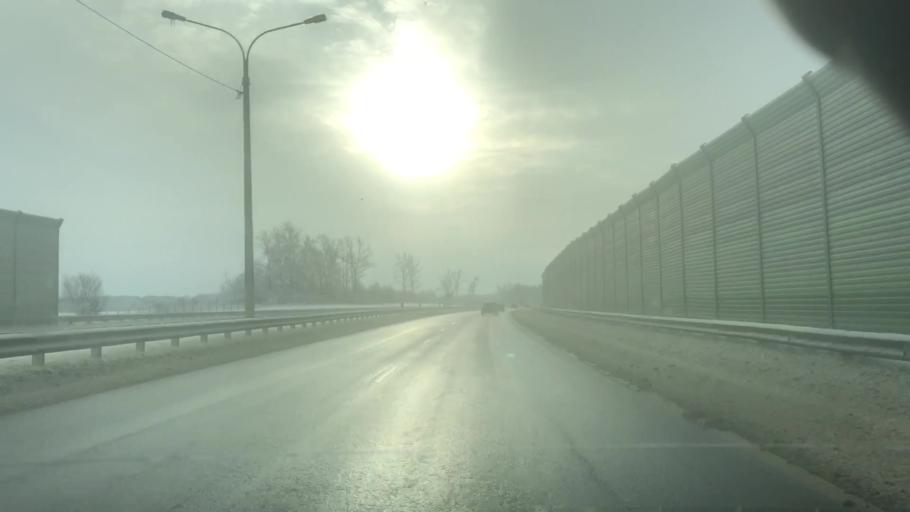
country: RU
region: Tula
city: Venev
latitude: 54.2753
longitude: 38.1605
